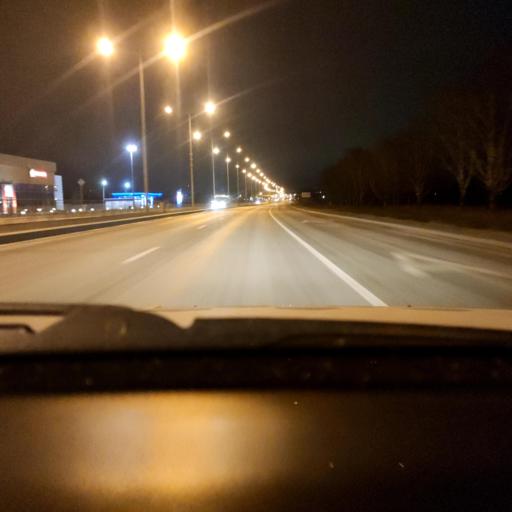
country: RU
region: Perm
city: Kondratovo
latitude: 57.9465
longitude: 56.0805
